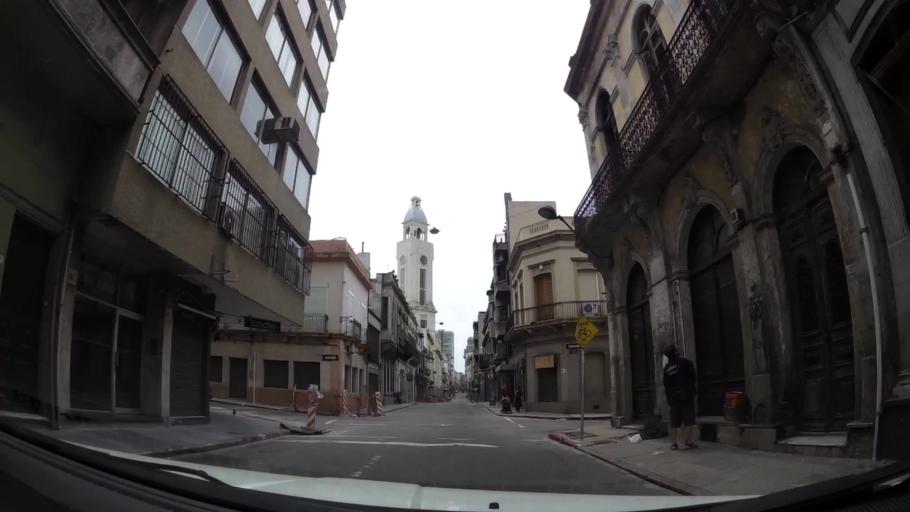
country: UY
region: Montevideo
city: Montevideo
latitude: -34.9091
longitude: -56.2067
